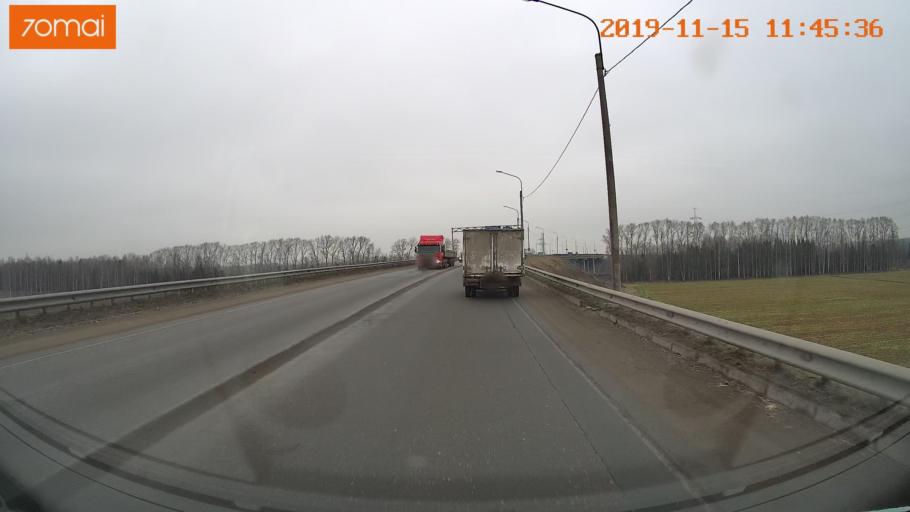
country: RU
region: Vologda
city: Molochnoye
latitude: 59.2417
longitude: 39.7695
